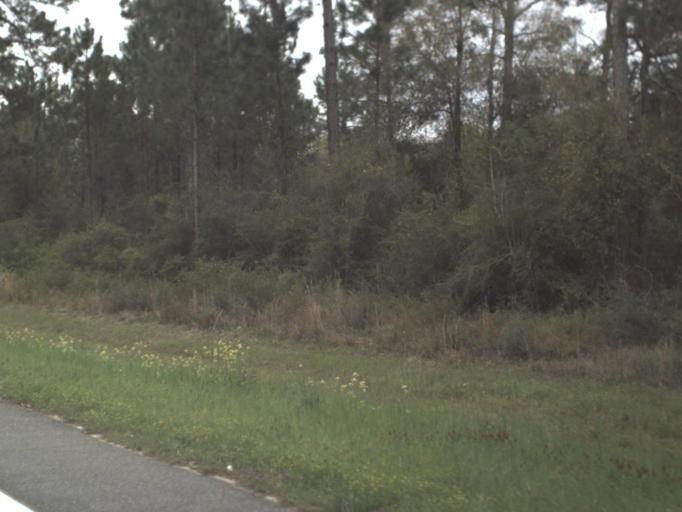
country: US
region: Florida
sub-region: Gulf County
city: Wewahitchka
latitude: 30.2400
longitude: -85.2169
